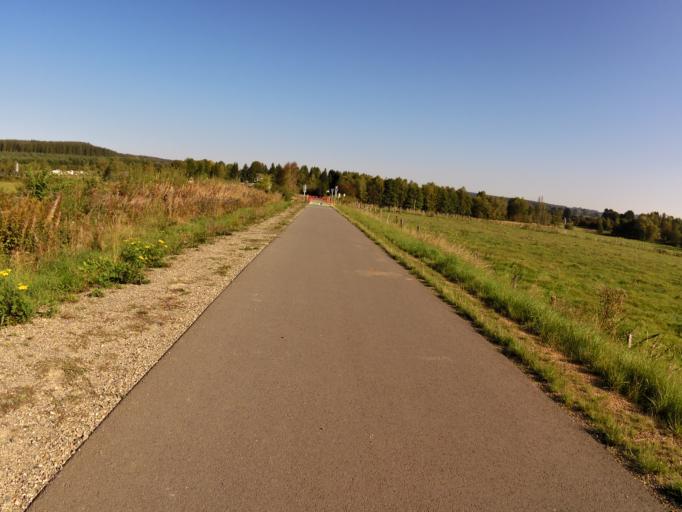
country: BE
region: Wallonia
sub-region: Province de Liege
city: Ambleve
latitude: 50.3440
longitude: 6.1204
